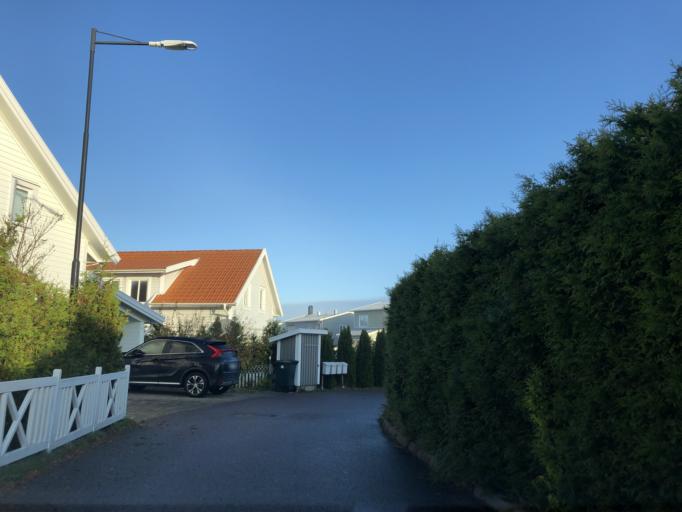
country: SE
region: Vaestra Goetaland
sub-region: Goteborg
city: Hammarkullen
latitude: 57.7896
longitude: 12.0505
